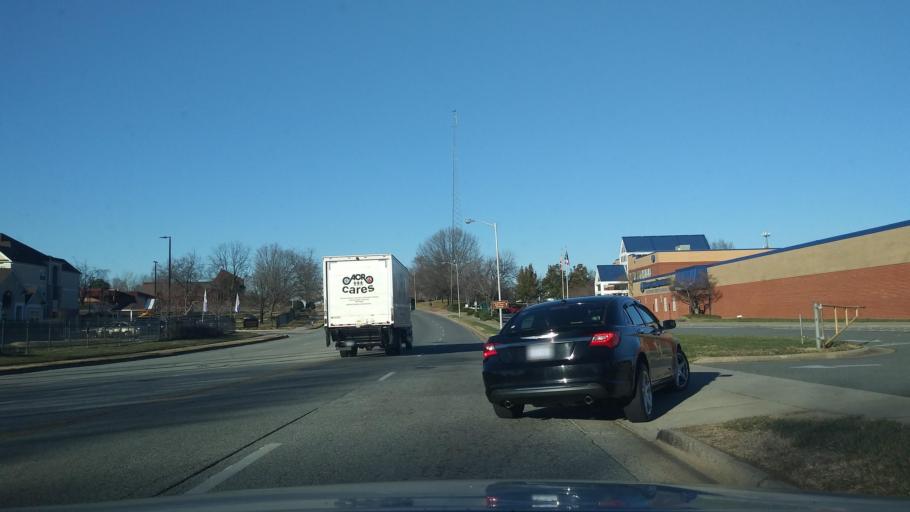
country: US
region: North Carolina
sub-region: Guilford County
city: Greensboro
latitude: 36.0593
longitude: -79.7935
